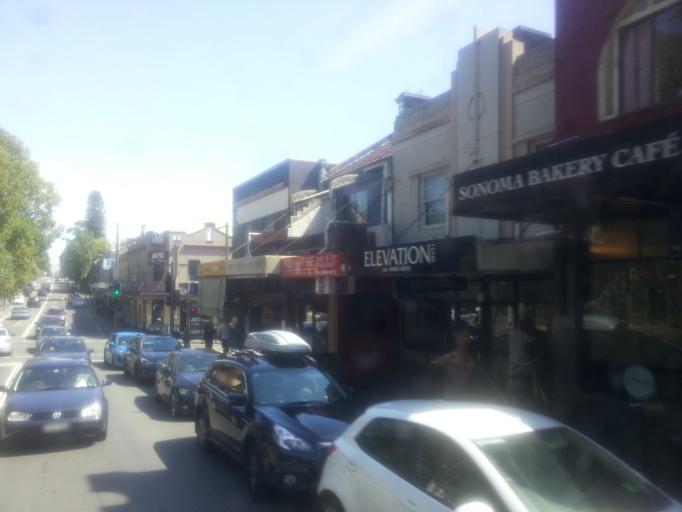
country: AU
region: New South Wales
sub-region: City of Sydney
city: Chippendale
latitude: -33.8800
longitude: 151.1872
